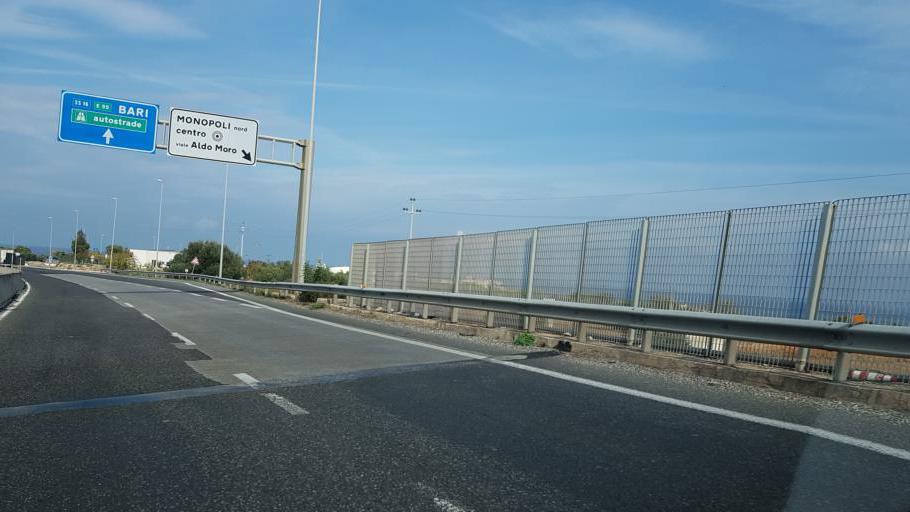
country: IT
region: Apulia
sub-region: Provincia di Bari
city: Monopoli
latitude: 40.9698
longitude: 17.2621
